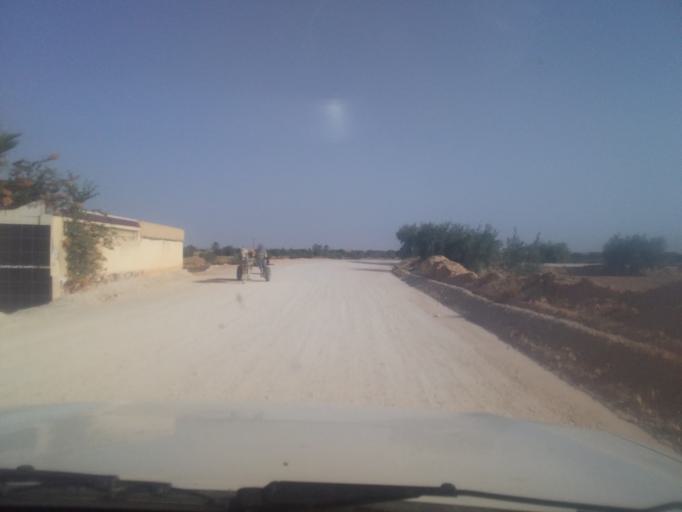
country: TN
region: Qabis
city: Matmata
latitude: 33.5938
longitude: 10.2718
